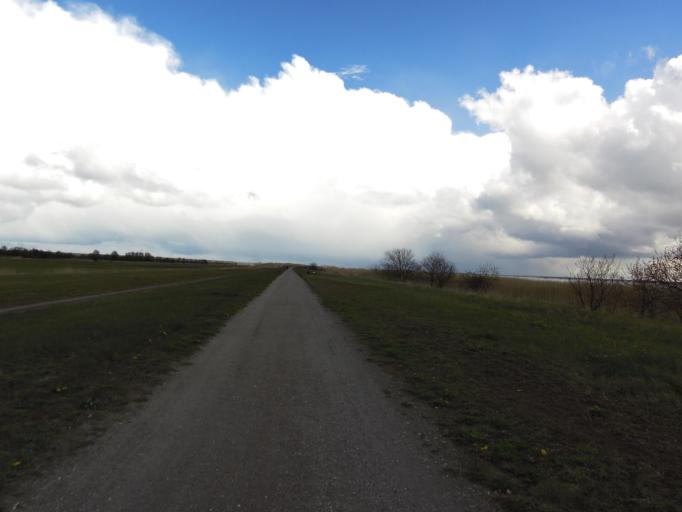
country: DE
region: Mecklenburg-Vorpommern
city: Born
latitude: 54.3819
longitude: 12.4602
